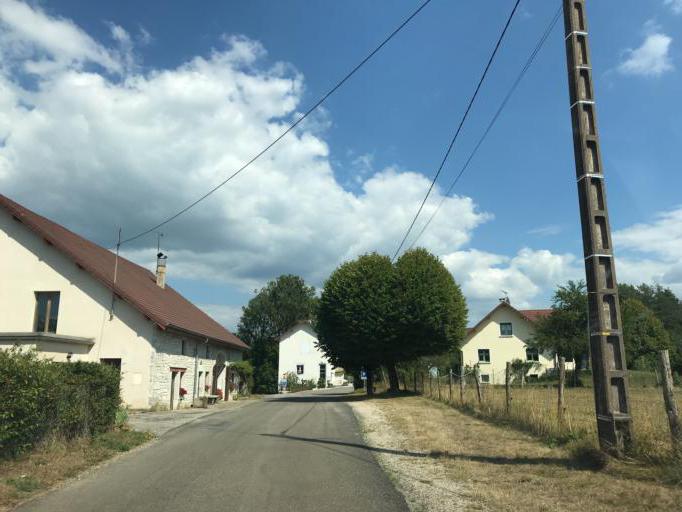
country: FR
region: Franche-Comte
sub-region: Departement du Jura
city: Clairvaux-les-Lacs
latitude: 46.5926
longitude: 5.7331
